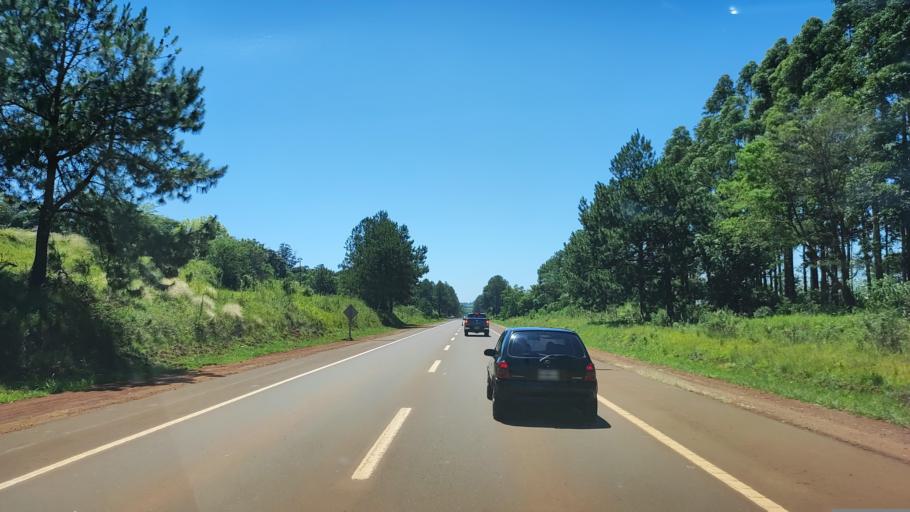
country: AR
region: Misiones
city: Aristobulo del Valle
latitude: -27.0842
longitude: -54.8084
